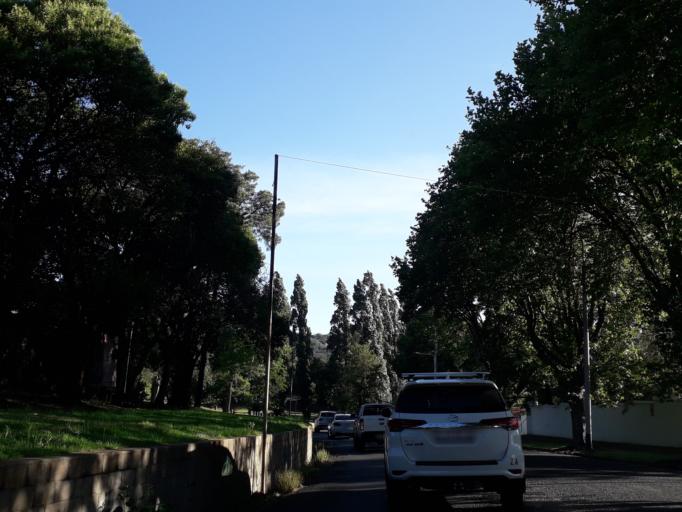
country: ZA
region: Gauteng
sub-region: City of Johannesburg Metropolitan Municipality
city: Johannesburg
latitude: -26.1550
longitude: 28.0286
